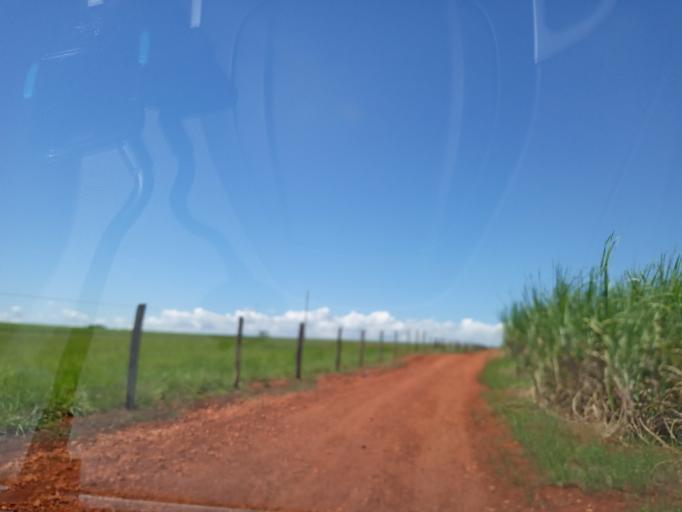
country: BR
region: Goias
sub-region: Itumbiara
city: Itumbiara
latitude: -18.3992
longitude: -49.1310
